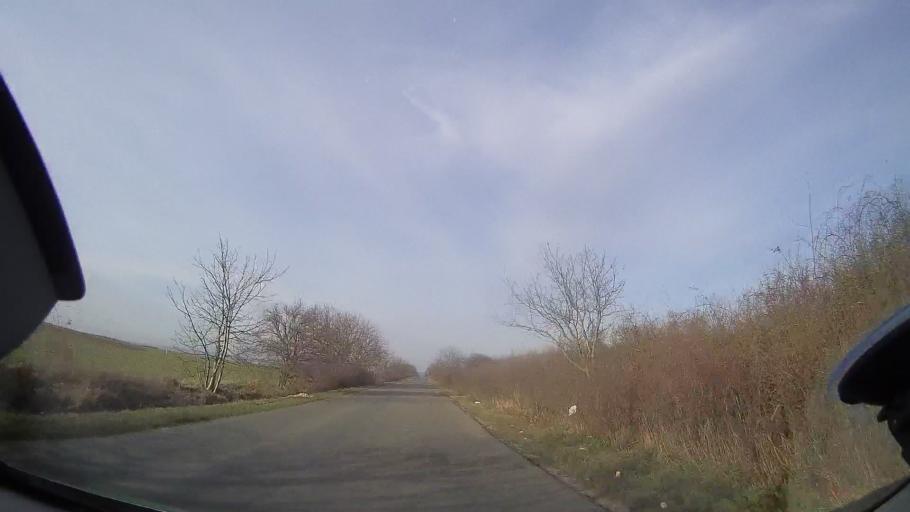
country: RO
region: Bihor
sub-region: Comuna Spinus
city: Spinus
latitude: 47.2175
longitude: 22.1742
